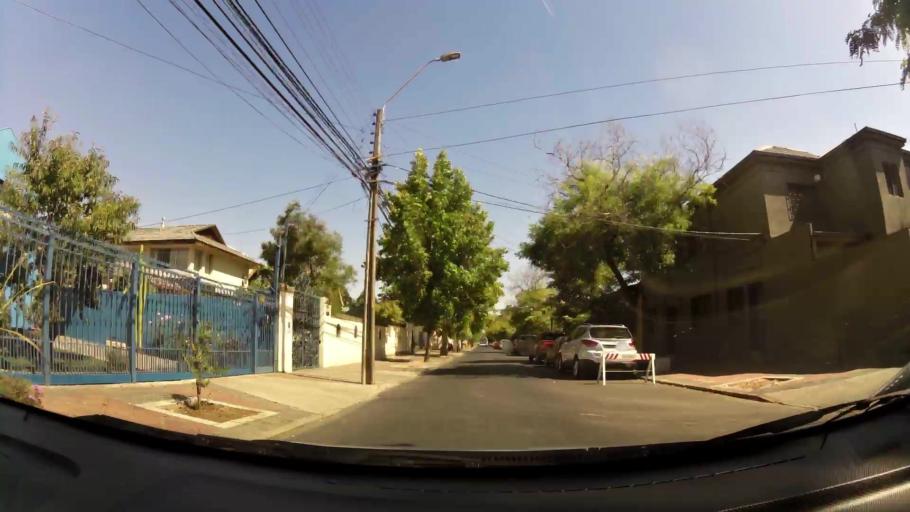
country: CL
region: Maule
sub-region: Provincia de Talca
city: Talca
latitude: -35.4203
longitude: -71.6593
